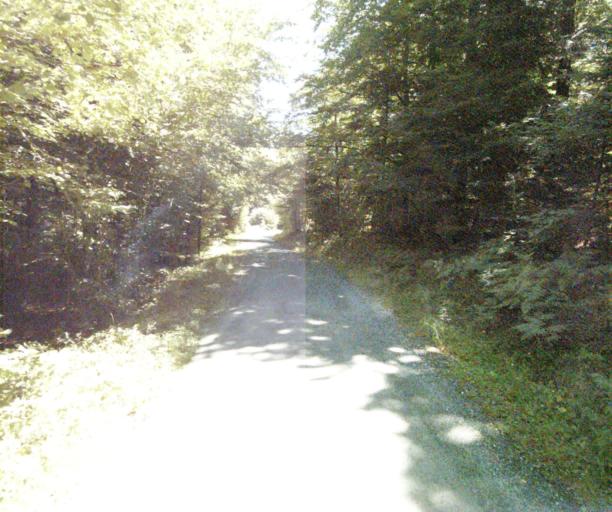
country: FR
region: Languedoc-Roussillon
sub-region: Departement de l'Aude
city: Cuxac-Cabardes
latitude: 43.3996
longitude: 2.2197
